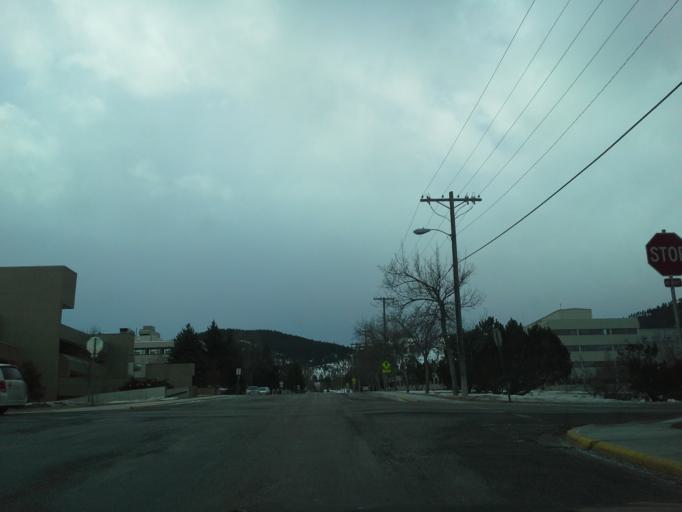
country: US
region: Montana
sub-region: Lewis and Clark County
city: Helena
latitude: 46.5870
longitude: -112.0147
